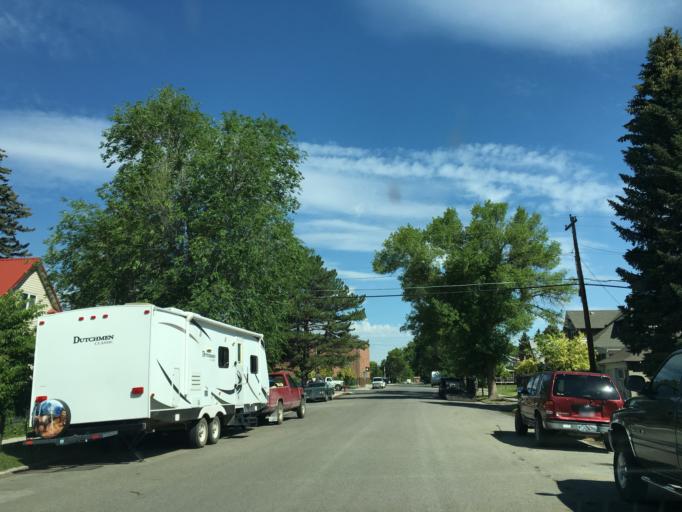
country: US
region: Montana
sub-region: Broadwater County
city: Townsend
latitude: 46.3206
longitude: -111.5143
